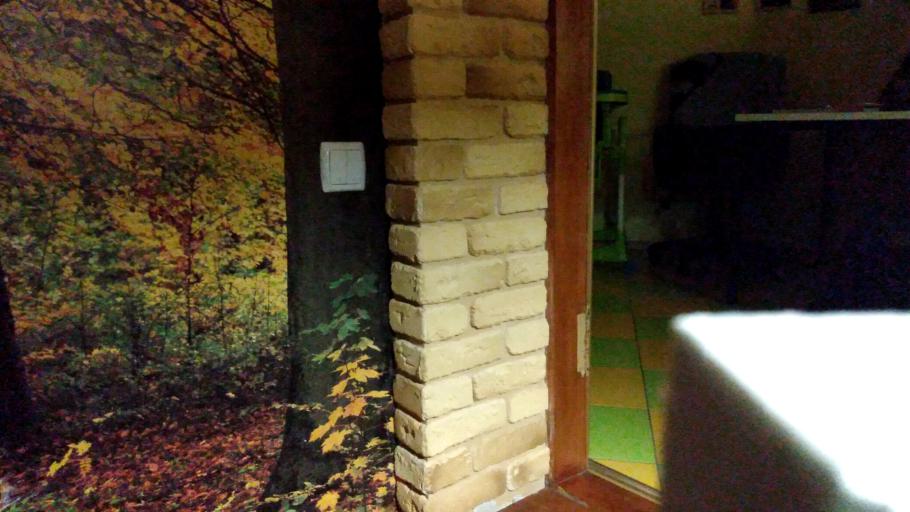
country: RU
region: Vologda
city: Lipin Bor
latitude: 60.8637
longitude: 38.0101
